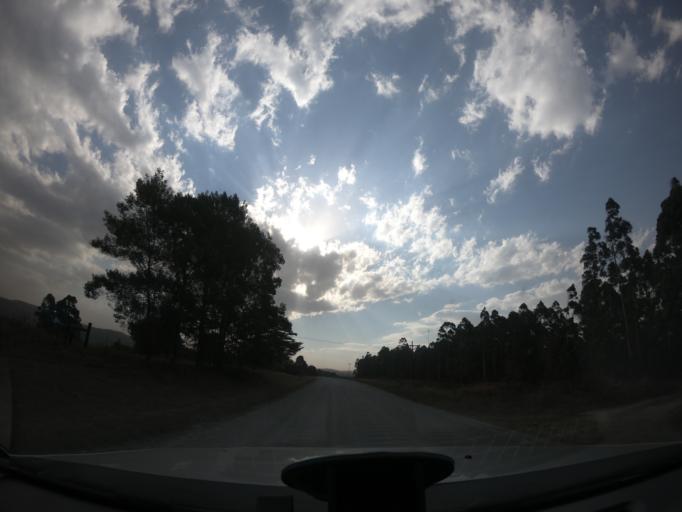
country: ZA
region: KwaZulu-Natal
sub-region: uMgungundlovu District Municipality
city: Howick
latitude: -29.4273
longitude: 30.1074
